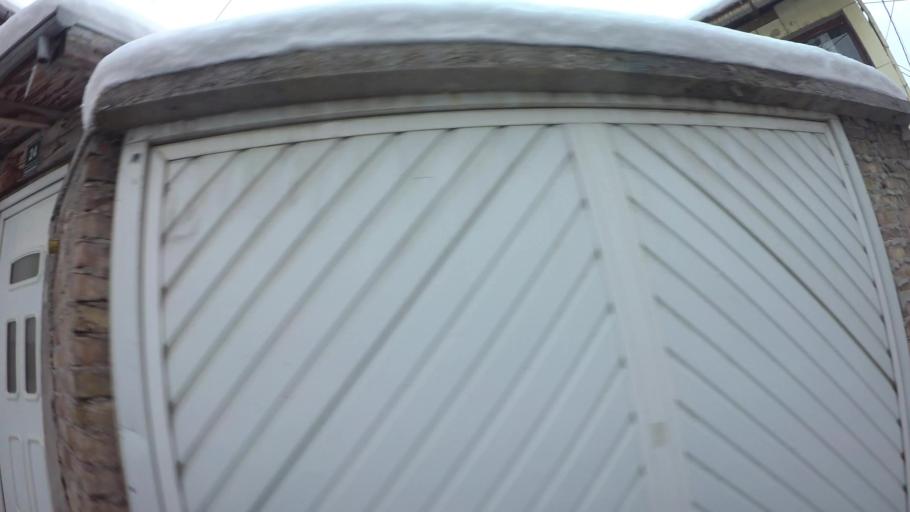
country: BA
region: Federation of Bosnia and Herzegovina
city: Kobilja Glava
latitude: 43.8649
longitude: 18.4324
